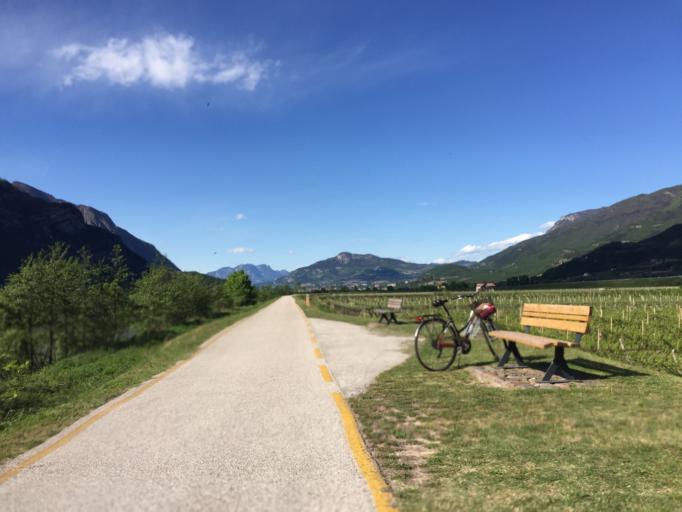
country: IT
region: Trentino-Alto Adige
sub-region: Provincia di Trento
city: Aldeno
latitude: 45.9783
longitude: 11.1100
